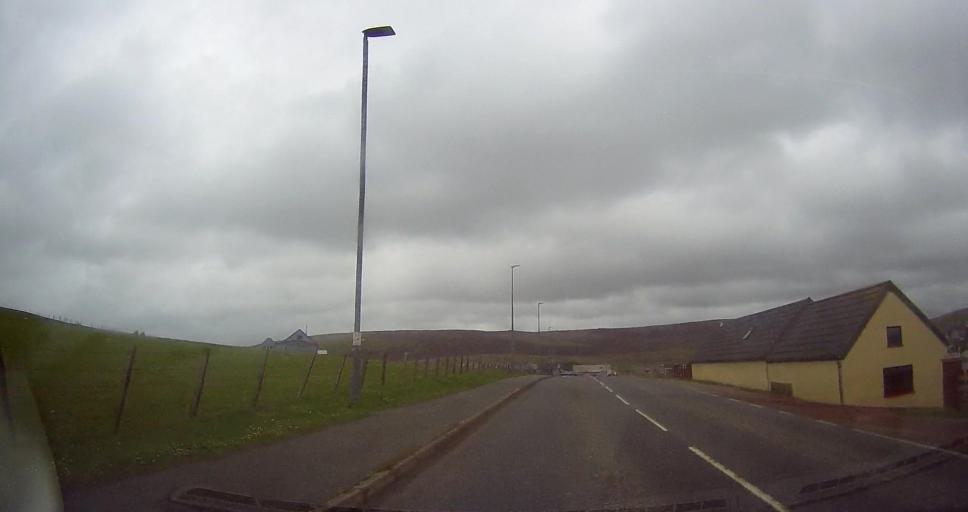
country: GB
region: Scotland
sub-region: Shetland Islands
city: Lerwick
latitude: 60.3945
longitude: -1.3614
